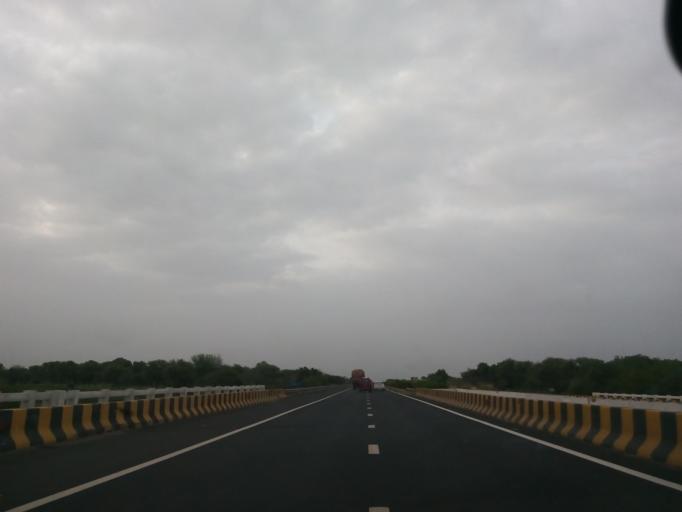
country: IN
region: Gujarat
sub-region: Kheda
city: Mahemdavad
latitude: 22.9081
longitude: 72.7681
